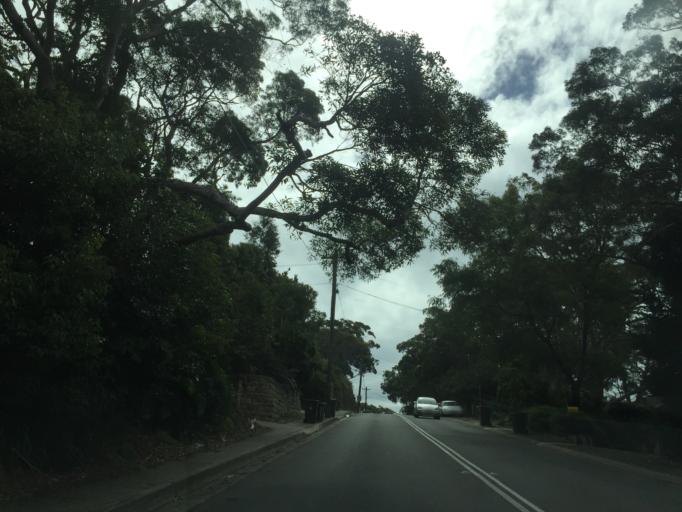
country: AU
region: New South Wales
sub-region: Pittwater
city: North Narrabeen
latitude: -33.7010
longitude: 151.2897
